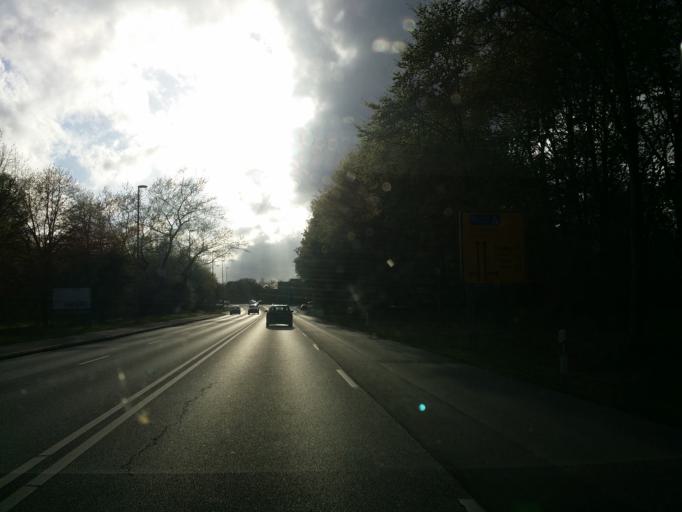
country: DE
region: Schleswig-Holstein
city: Rendsburg
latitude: 54.2943
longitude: 9.6595
